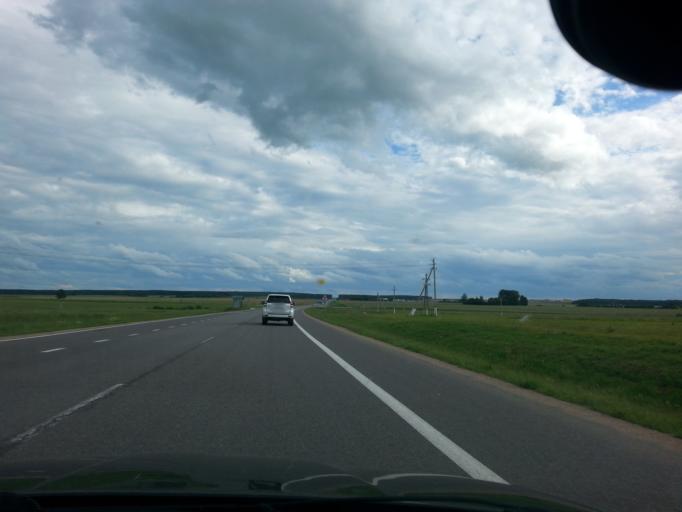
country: BY
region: Grodnenskaya
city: Astravyets
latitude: 54.7366
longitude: 26.0874
